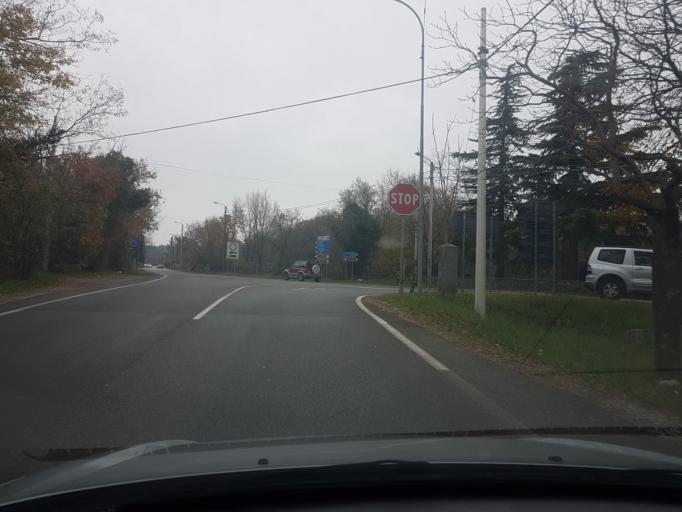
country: IT
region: Friuli Venezia Giulia
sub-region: Provincia di Trieste
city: Prosecco-Contovello
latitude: 45.7150
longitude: 13.7279
